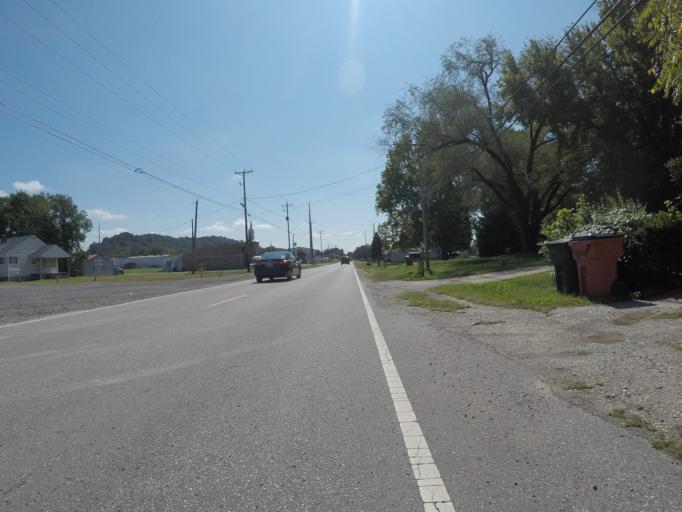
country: US
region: Kentucky
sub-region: Boyd County
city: Ashland
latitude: 38.4648
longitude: -82.6019
